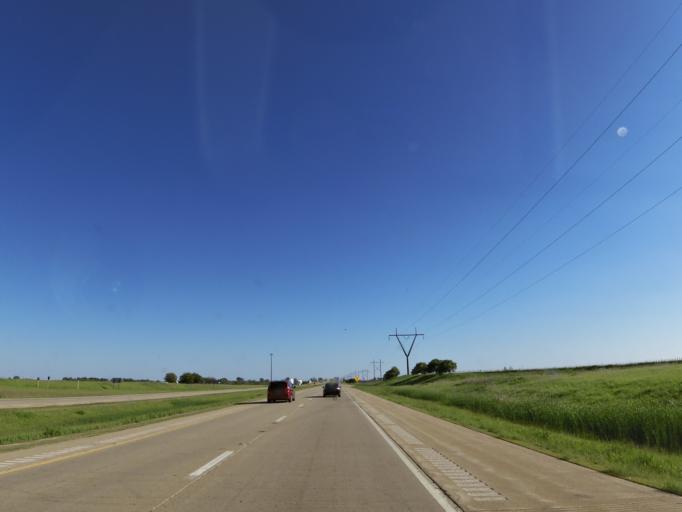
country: US
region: Illinois
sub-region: Marshall County
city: Wenona
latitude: 41.0273
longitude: -89.0566
